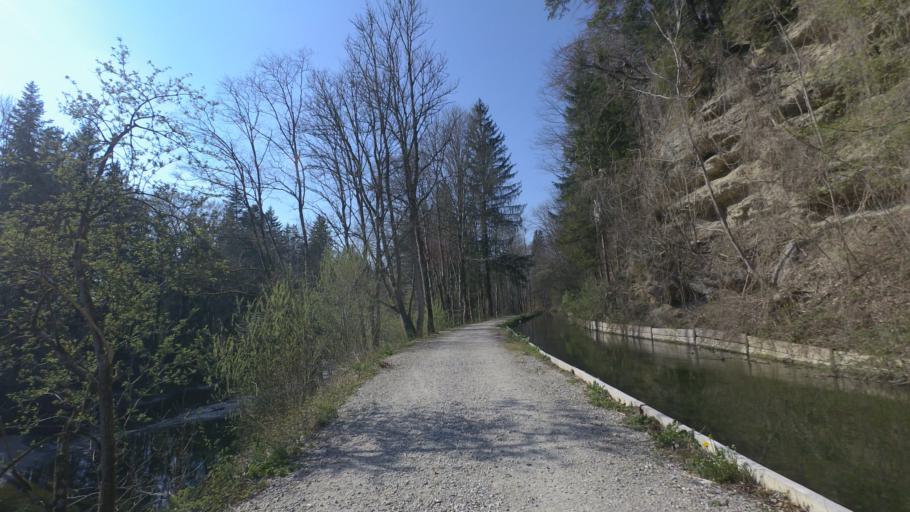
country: DE
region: Bavaria
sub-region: Upper Bavaria
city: Traunreut
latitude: 47.9602
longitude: 12.5766
